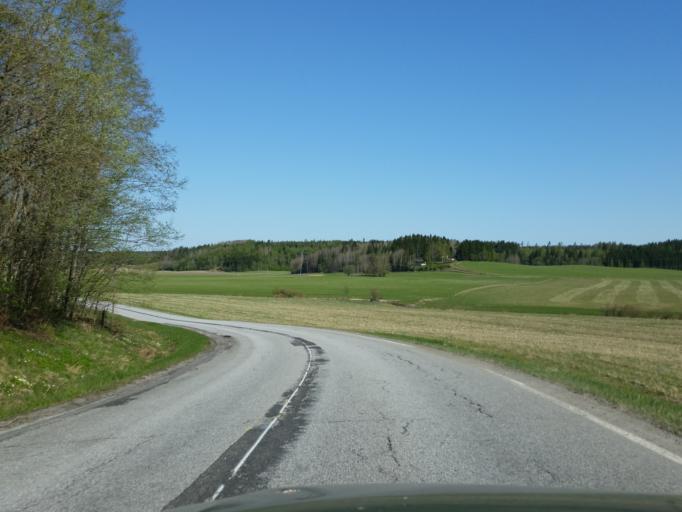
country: FI
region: Uusimaa
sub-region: Helsinki
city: Siuntio
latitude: 60.1726
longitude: 24.1626
